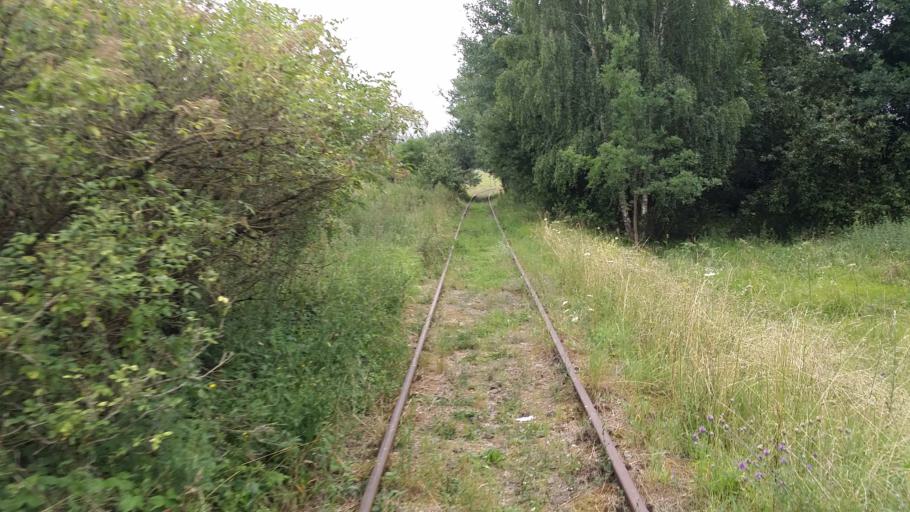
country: PL
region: West Pomeranian Voivodeship
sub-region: Powiat choszczenski
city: Drawno
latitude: 53.2090
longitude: 15.7624
